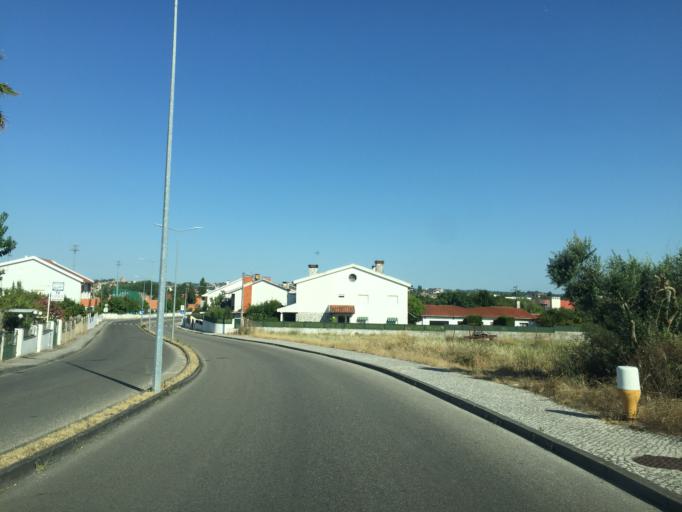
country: PT
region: Santarem
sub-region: Tomar
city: Tomar
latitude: 39.5995
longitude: -8.3854
